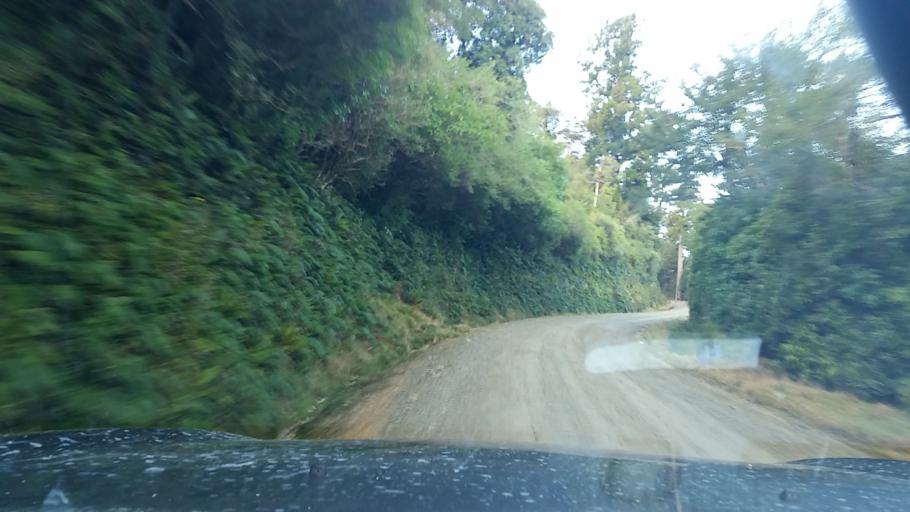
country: NZ
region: Marlborough
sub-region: Marlborough District
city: Picton
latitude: -41.0992
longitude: 174.1323
